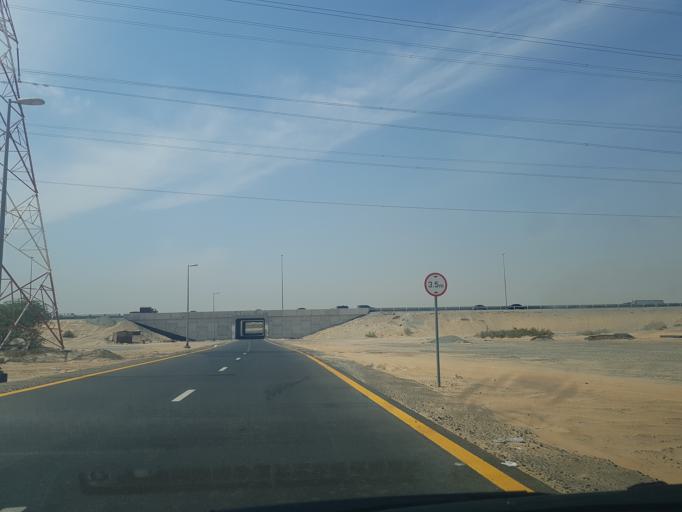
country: AE
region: Ash Shariqah
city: Sharjah
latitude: 25.2865
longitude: 55.5903
